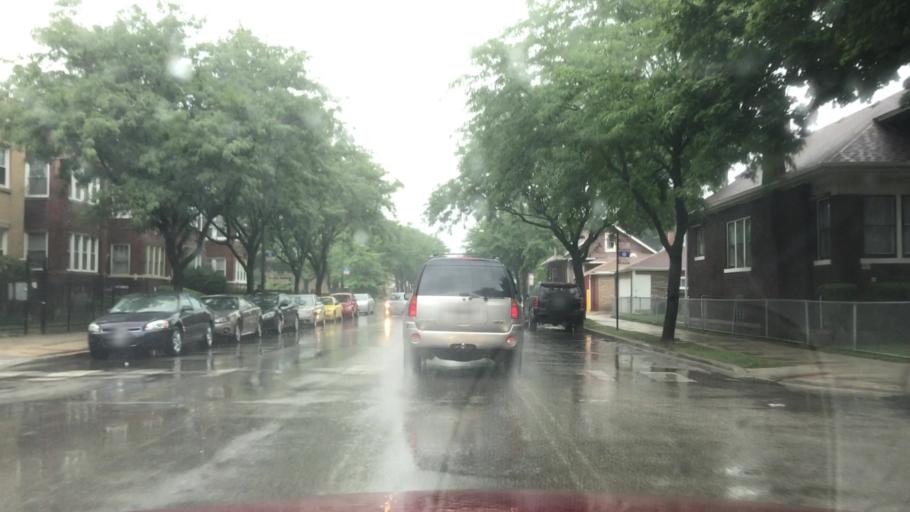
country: US
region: Illinois
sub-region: Cook County
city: Oak Park
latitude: 41.9031
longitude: -87.7558
